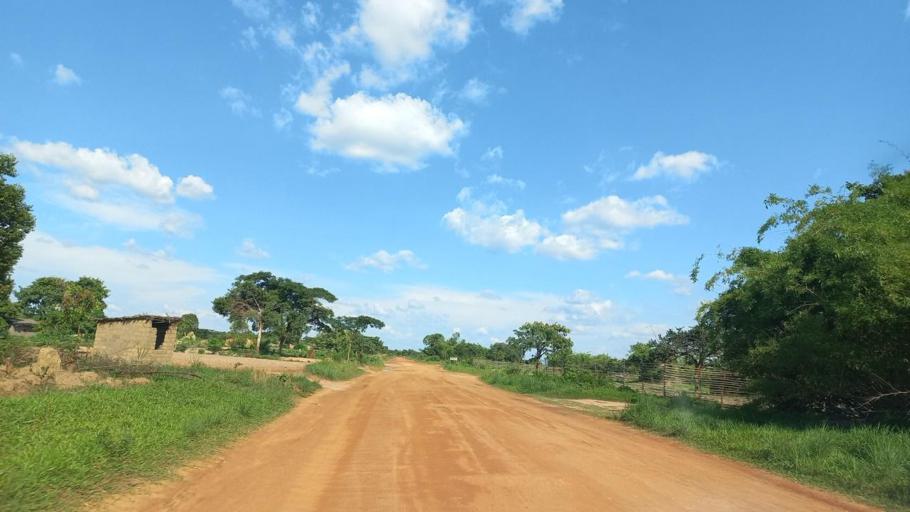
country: ZM
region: Copperbelt
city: Kitwe
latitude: -12.8701
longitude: 28.3551
